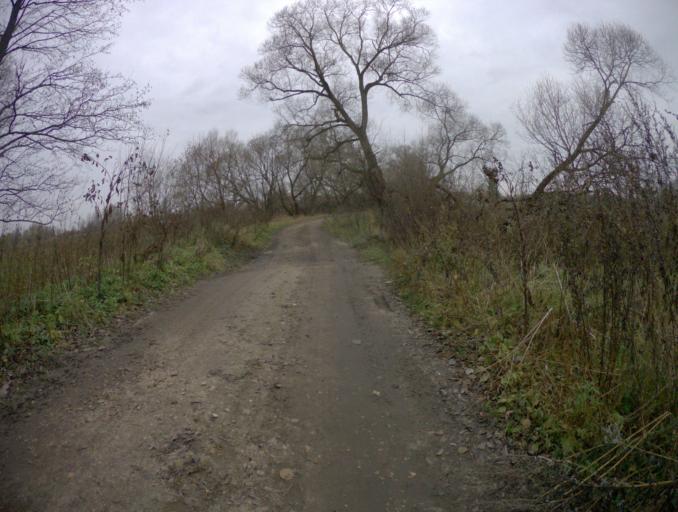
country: RU
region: Vladimir
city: Krasnyy Oktyabr'
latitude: 55.9979
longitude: 38.8629
